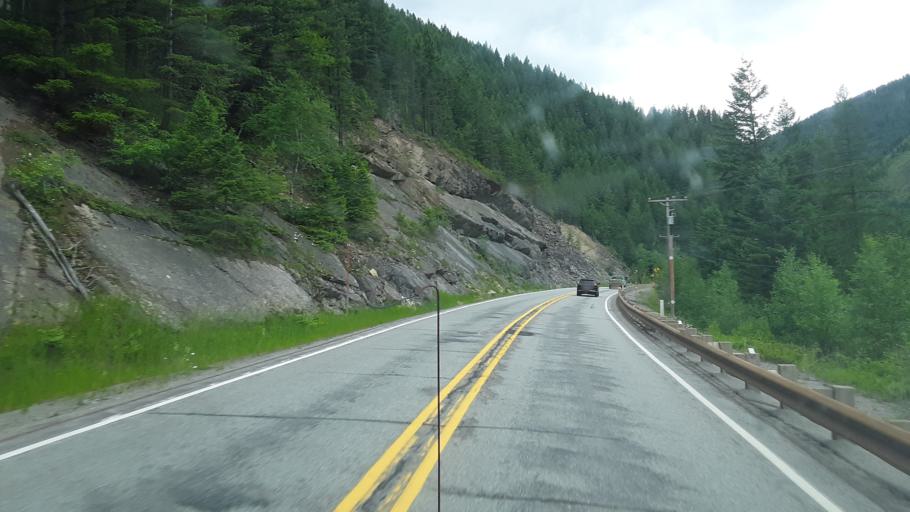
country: US
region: Montana
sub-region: Flathead County
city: Columbia Falls
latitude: 48.4939
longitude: -113.9146
